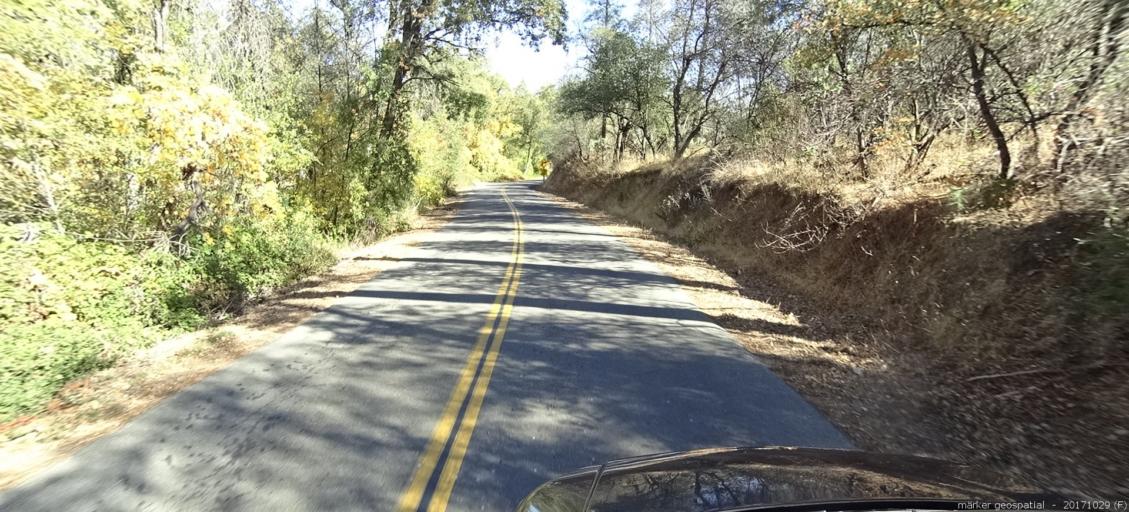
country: US
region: California
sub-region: Shasta County
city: Shasta
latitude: 40.4817
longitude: -122.6343
